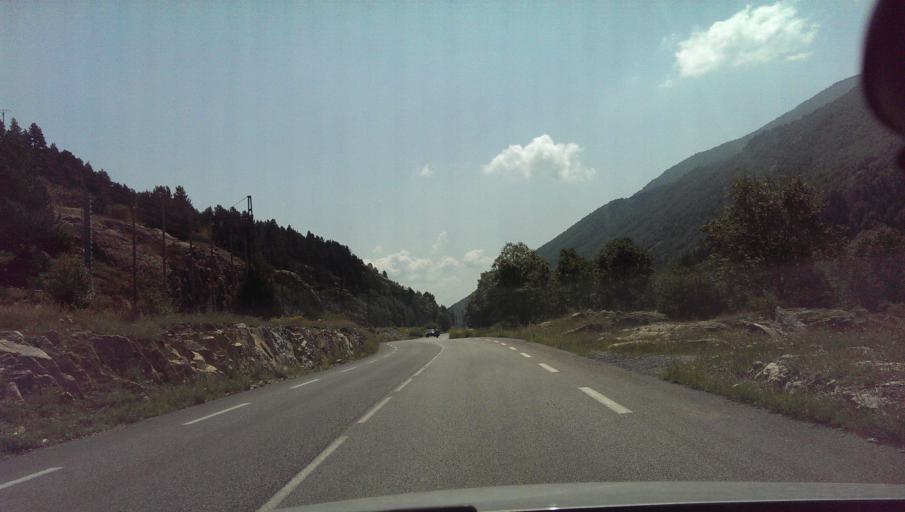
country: ES
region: Catalonia
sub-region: Provincia de Girona
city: Guils de Cerdanya
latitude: 42.5068
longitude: 1.8332
